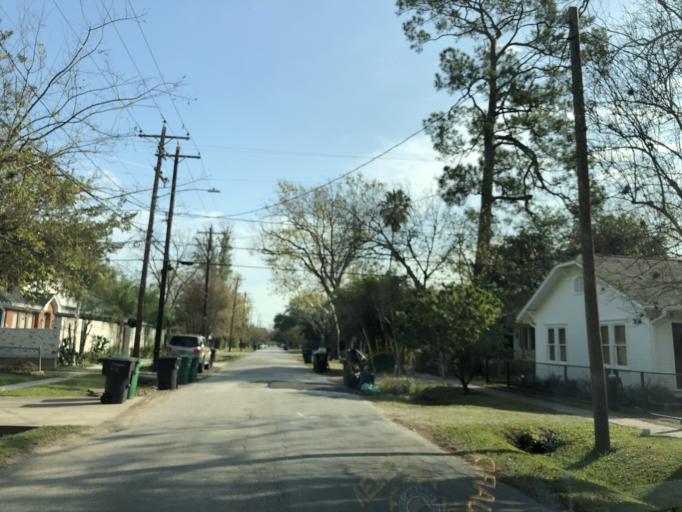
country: US
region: Texas
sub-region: Harris County
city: Houston
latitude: 29.7926
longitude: -95.3953
